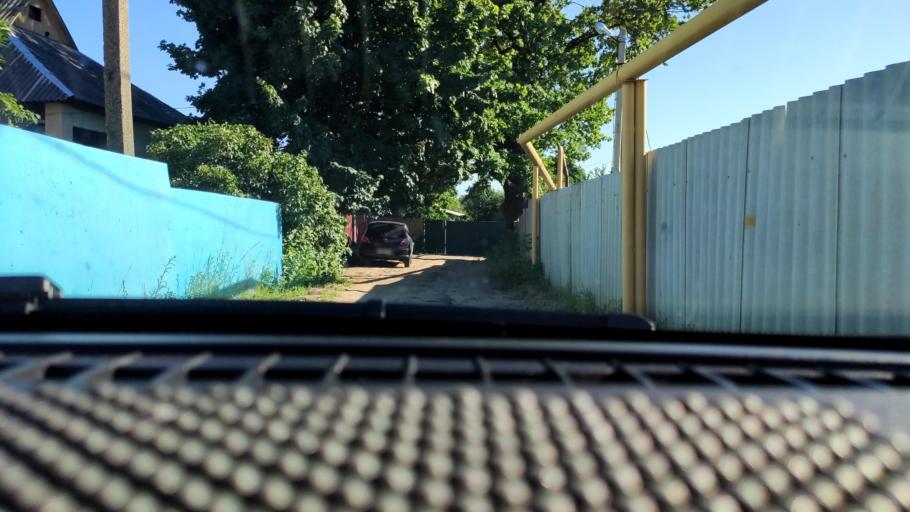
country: RU
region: Voronezj
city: Podgornoye
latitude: 51.7391
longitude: 39.1516
